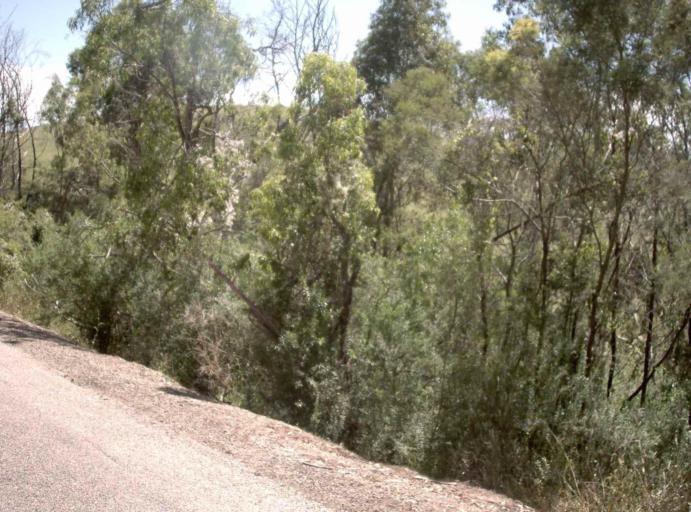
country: AU
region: Victoria
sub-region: East Gippsland
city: Lakes Entrance
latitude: -37.4509
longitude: 148.1923
